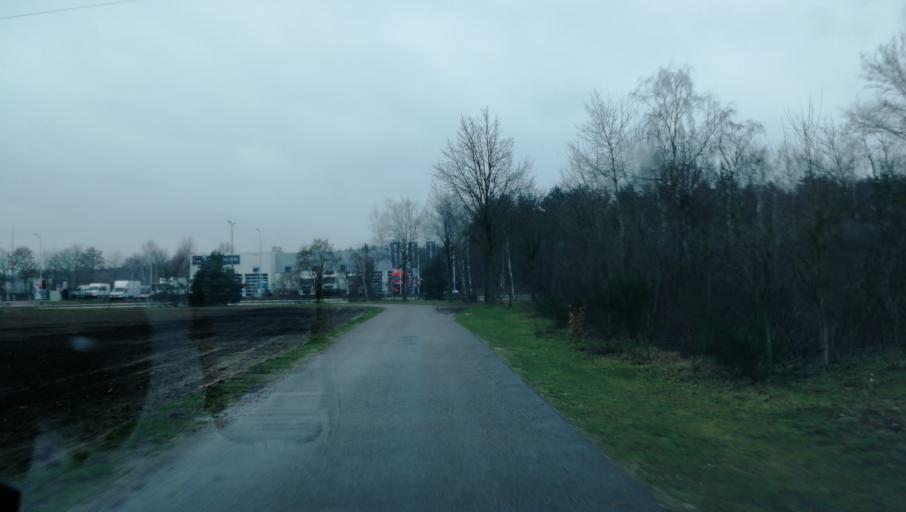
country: NL
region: Limburg
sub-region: Gemeente Venlo
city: Tegelen
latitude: 51.3880
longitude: 6.1163
